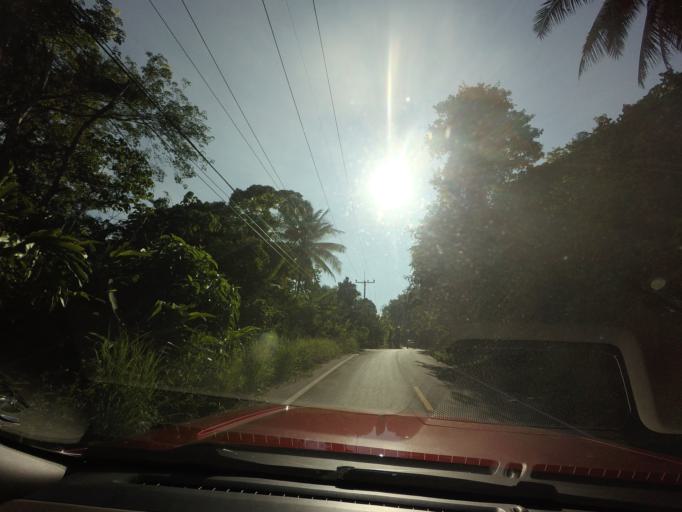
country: TH
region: Yala
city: Than To
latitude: 6.0704
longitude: 101.3496
